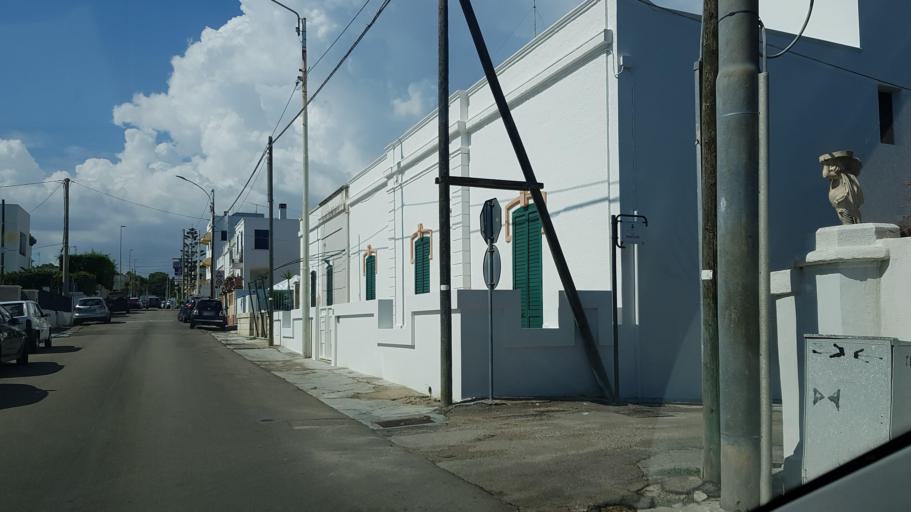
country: IT
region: Apulia
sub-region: Provincia di Lecce
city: Leuca
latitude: 39.8004
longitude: 18.3579
